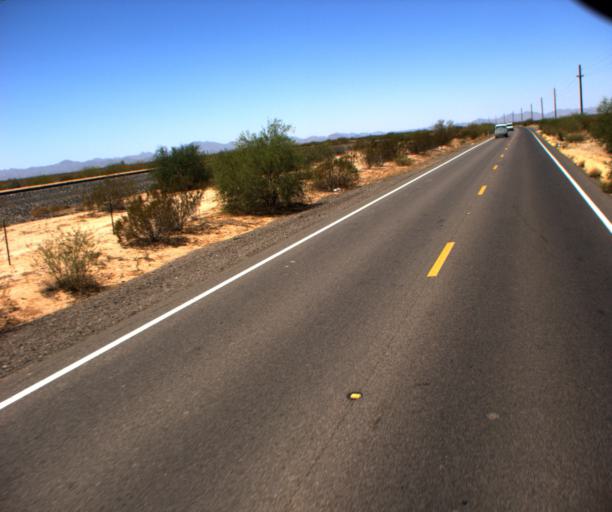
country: US
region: Arizona
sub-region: Pinal County
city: Maricopa
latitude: 33.0709
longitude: -112.2086
